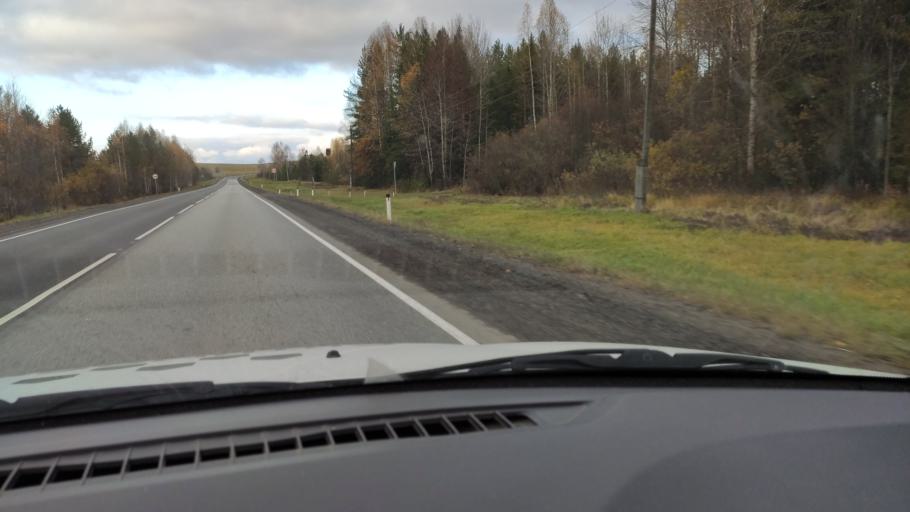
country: RU
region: Kirov
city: Belaya Kholunitsa
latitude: 58.8860
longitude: 50.8740
